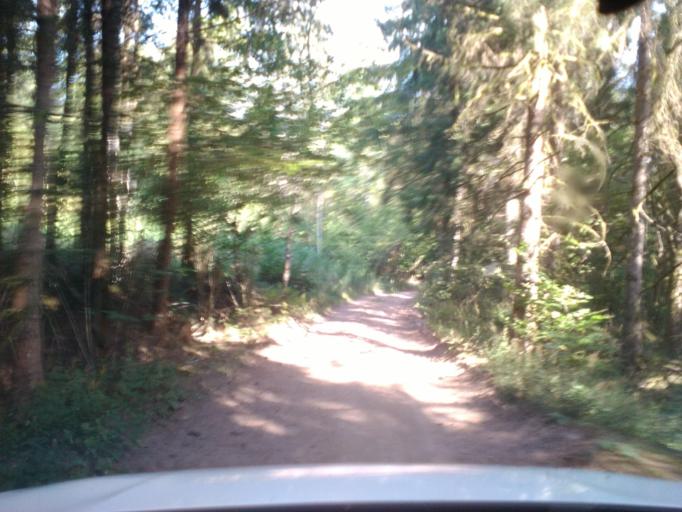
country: FR
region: Lorraine
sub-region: Departement des Vosges
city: Senones
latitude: 48.3618
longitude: 6.9940
